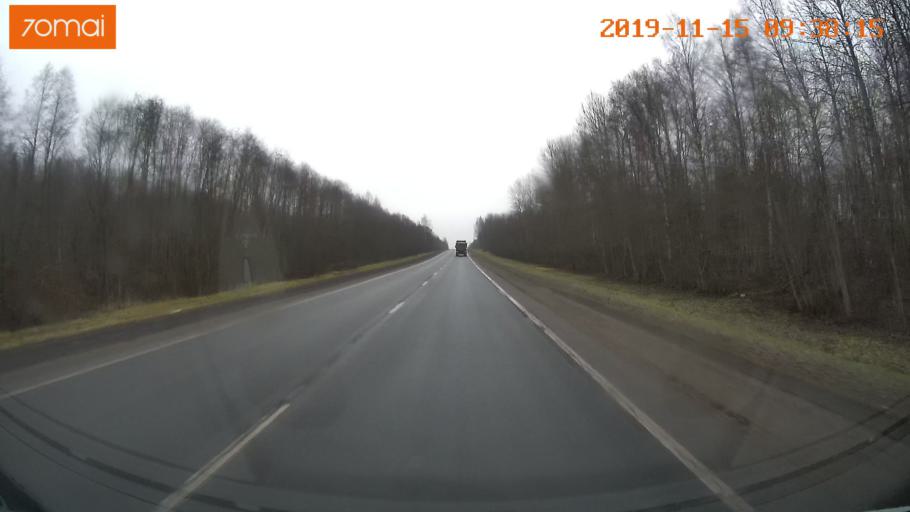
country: RU
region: Vologda
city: Sheksna
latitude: 59.2336
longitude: 38.4520
